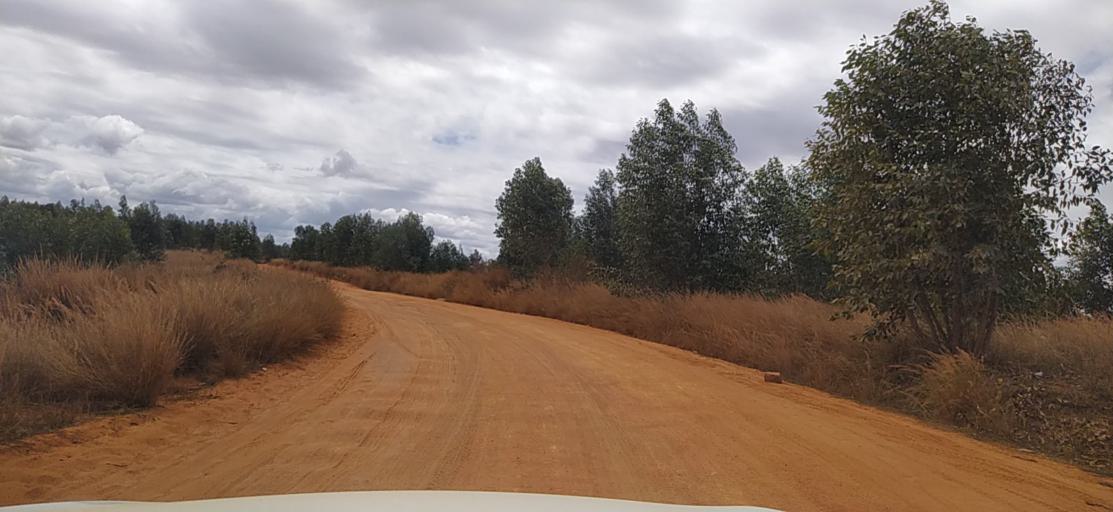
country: MG
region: Alaotra Mangoro
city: Ambatondrazaka
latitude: -18.0433
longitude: 48.2497
